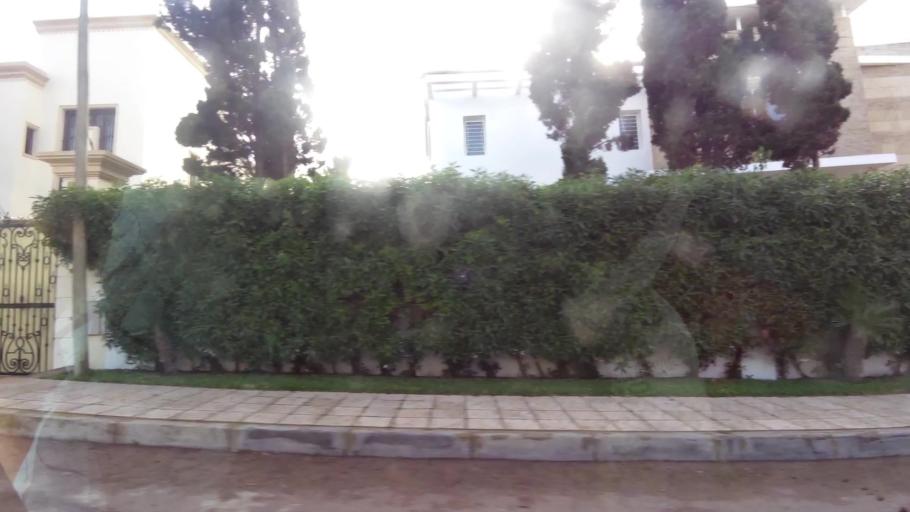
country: MA
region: Grand Casablanca
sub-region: Casablanca
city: Casablanca
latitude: 33.5759
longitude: -7.6986
